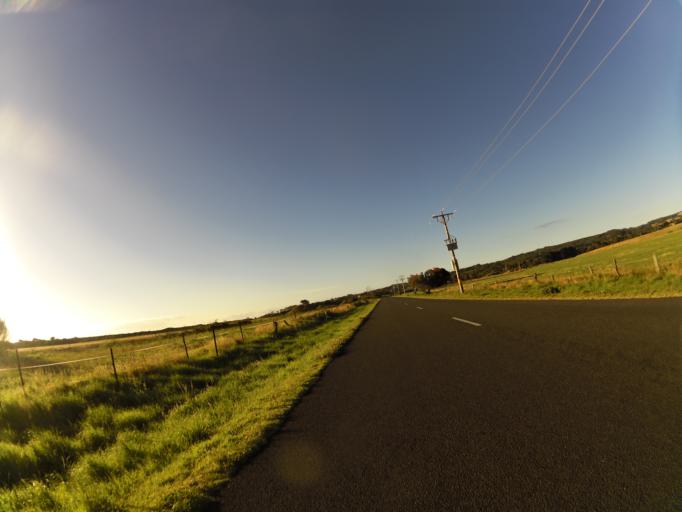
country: AU
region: Victoria
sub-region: Colac-Otway
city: Apollo Bay
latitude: -38.7632
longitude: 143.6616
